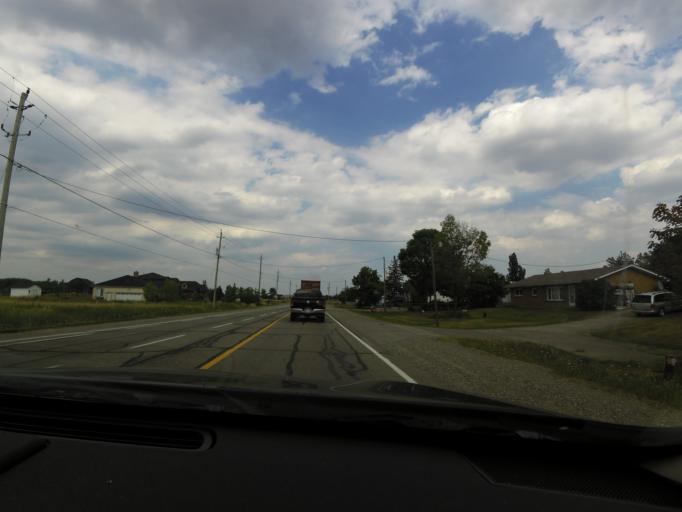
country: CA
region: Ontario
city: Brampton
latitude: 43.7744
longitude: -79.8772
